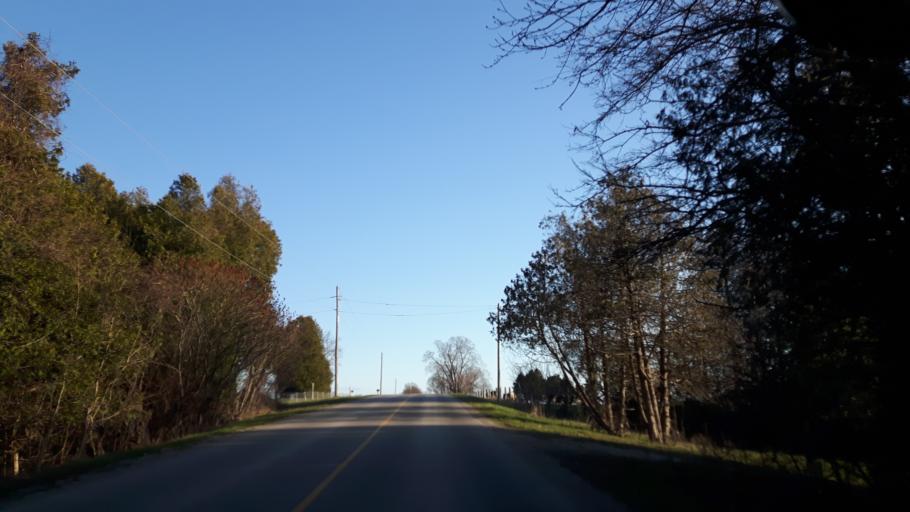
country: CA
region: Ontario
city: Goderich
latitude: 43.6673
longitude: -81.6847
